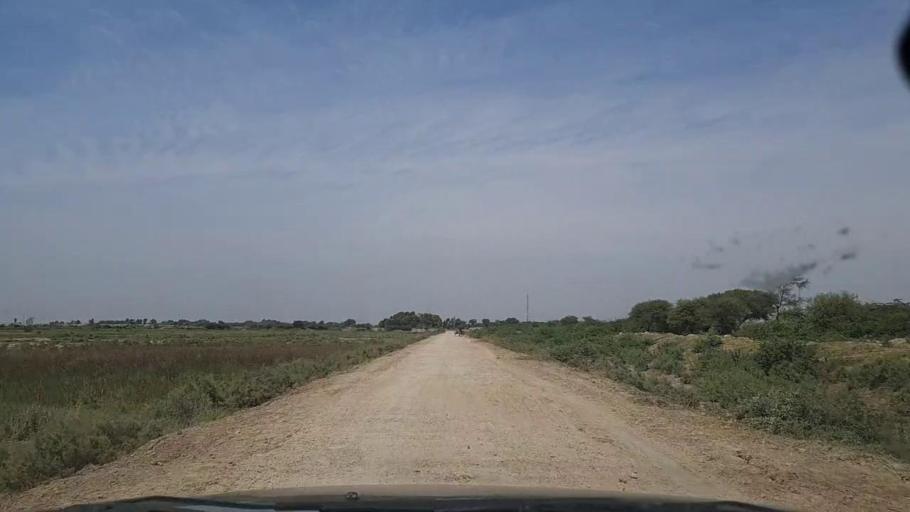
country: PK
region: Sindh
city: Mirpur Batoro
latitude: 24.6505
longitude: 68.1832
